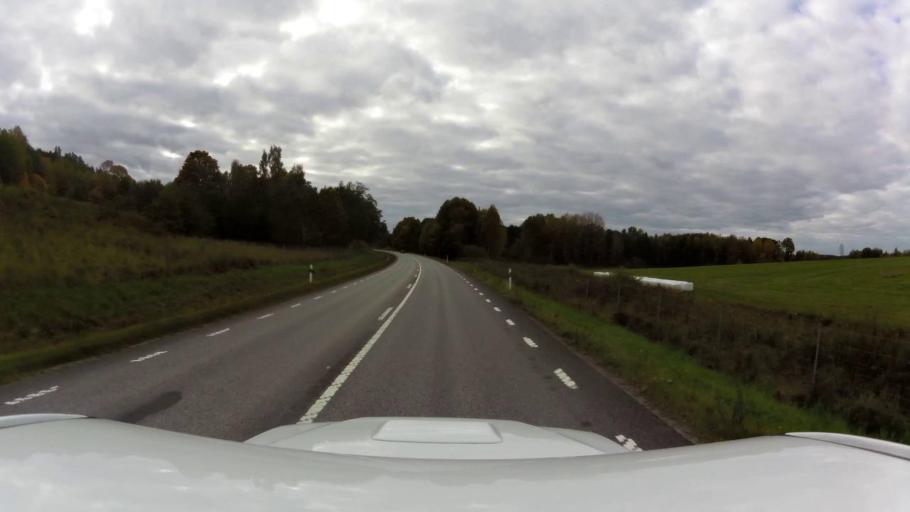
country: SE
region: OEstergoetland
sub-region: Kinda Kommun
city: Rimforsa
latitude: 58.1894
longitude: 15.6665
